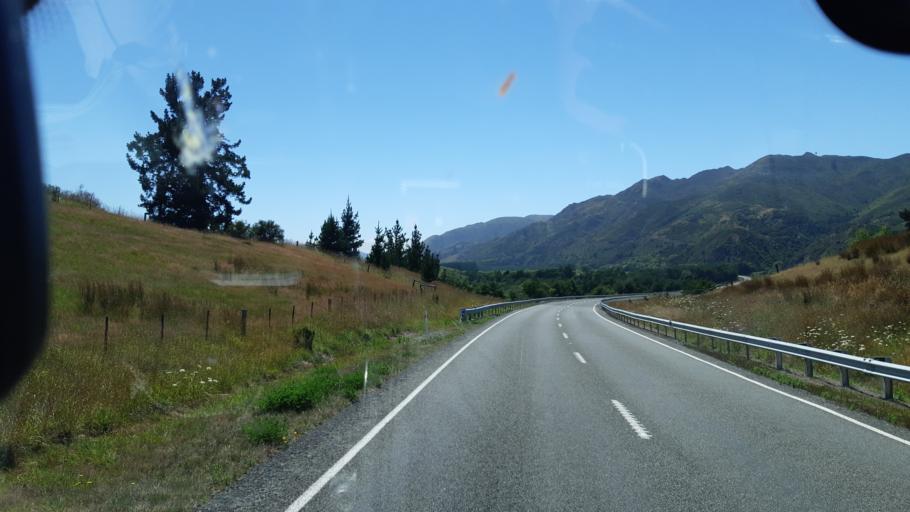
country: NZ
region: Canterbury
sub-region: Kaikoura District
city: Kaikoura
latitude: -42.6370
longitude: 173.3281
